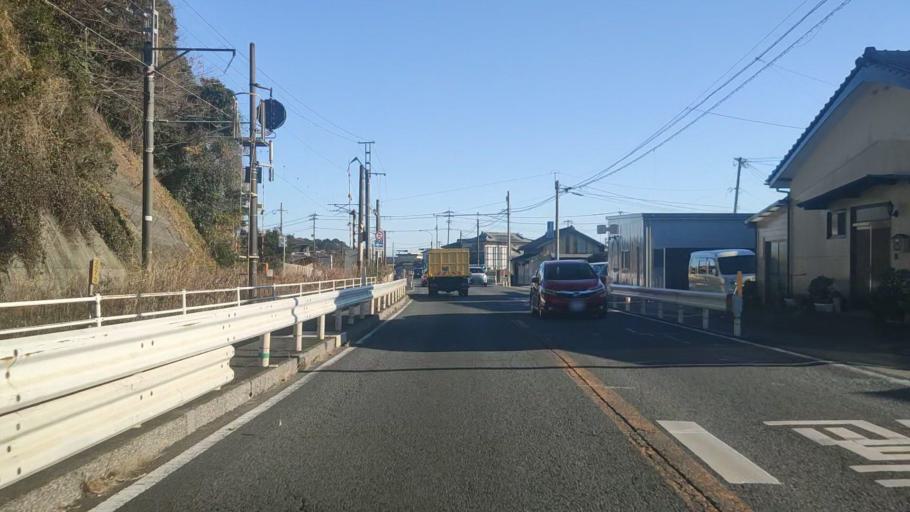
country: JP
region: Miyazaki
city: Nobeoka
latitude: 32.5108
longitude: 131.6799
